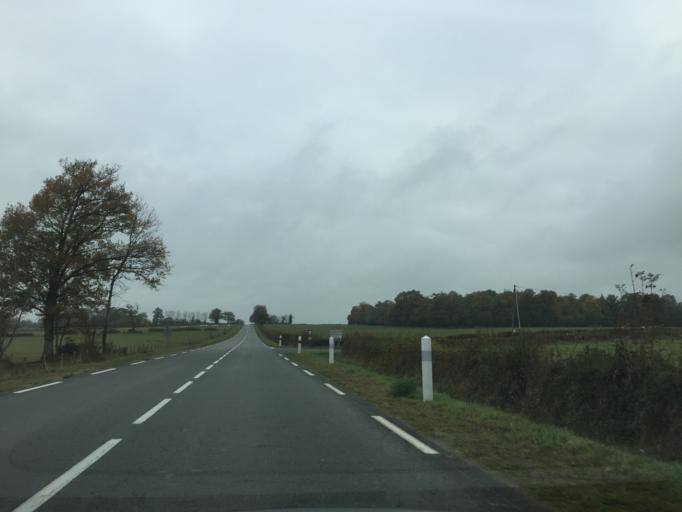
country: FR
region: Limousin
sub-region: Departement de la Creuse
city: Gouzon
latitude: 46.1347
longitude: 2.1946
